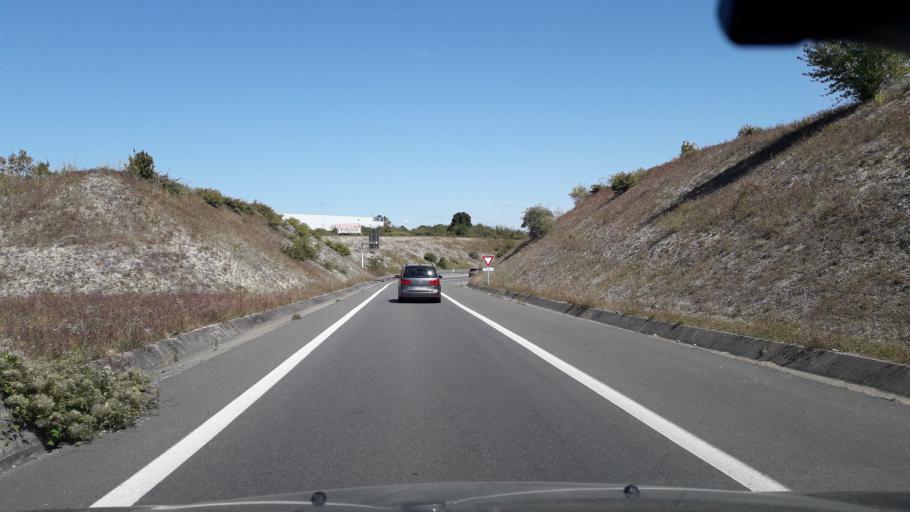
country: FR
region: Poitou-Charentes
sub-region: Departement de la Charente
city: Gond-Pontouvre
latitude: 45.6742
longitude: 0.1445
